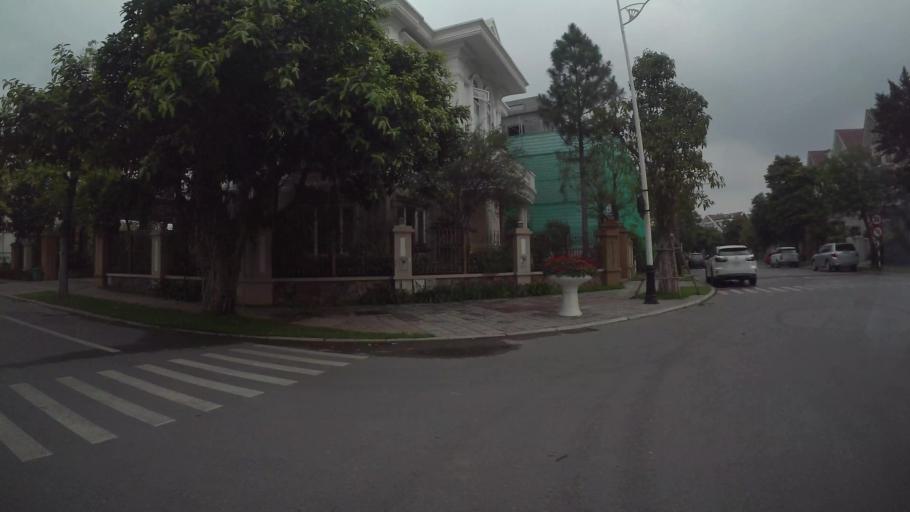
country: VN
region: Ha Noi
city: Trau Quy
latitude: 21.0399
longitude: 105.9202
